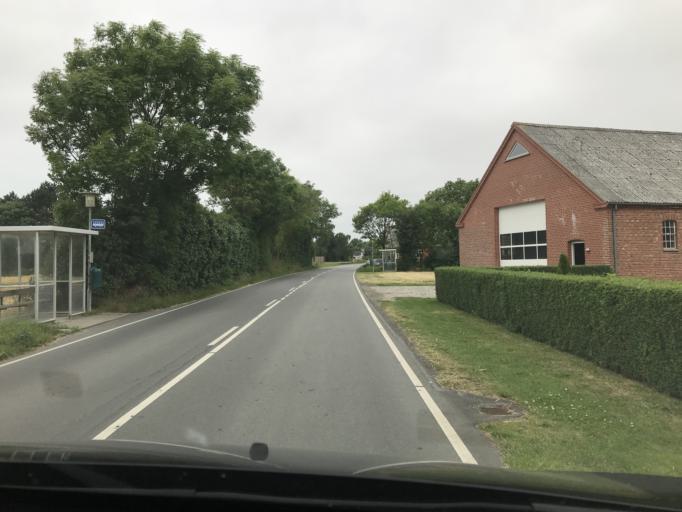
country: DK
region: South Denmark
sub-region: AEro Kommune
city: AEroskobing
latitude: 54.8612
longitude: 10.3803
